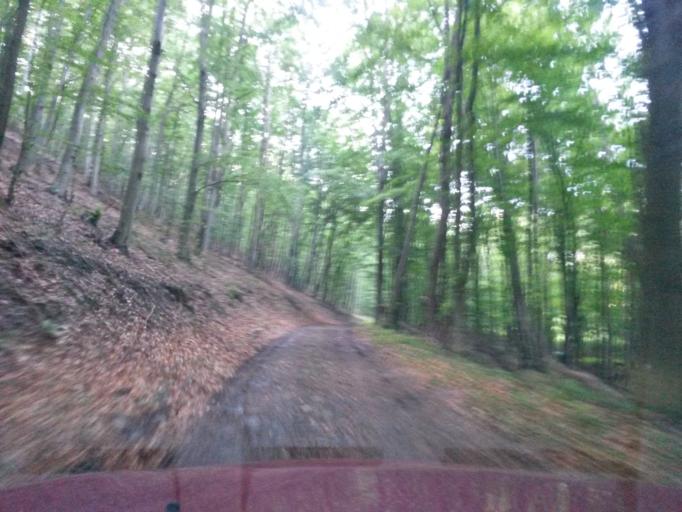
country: SK
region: Kosicky
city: Moldava nad Bodvou
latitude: 48.7377
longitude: 21.0640
